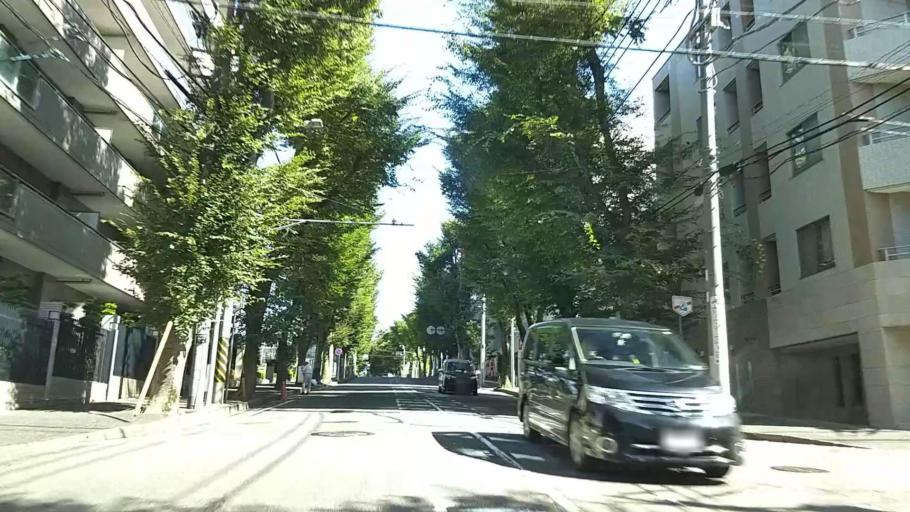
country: JP
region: Tokyo
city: Chofugaoka
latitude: 35.5742
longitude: 139.5553
